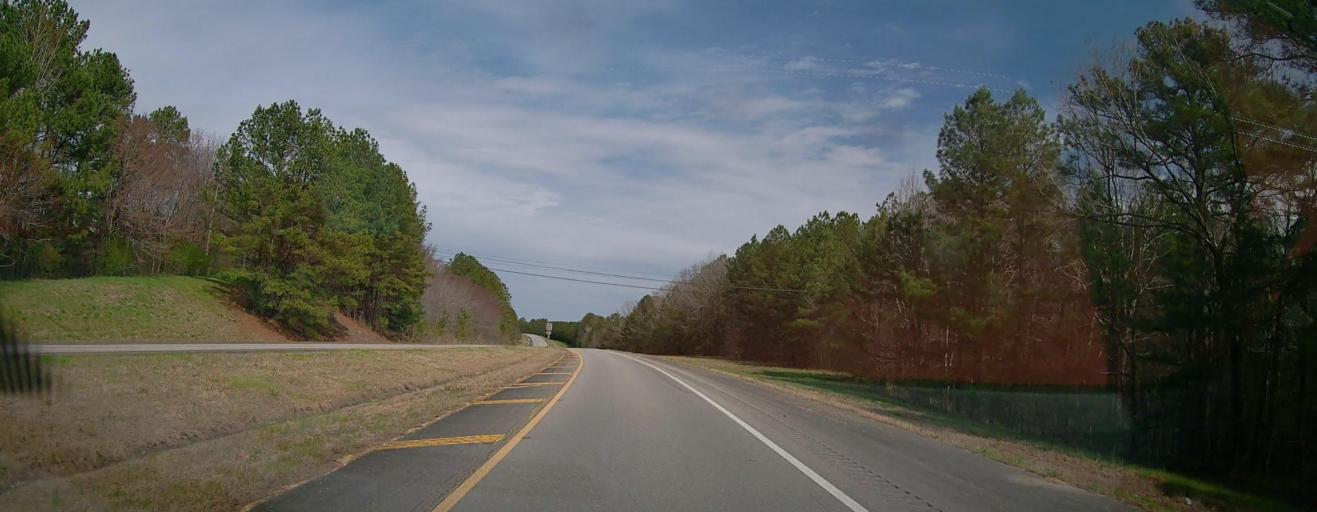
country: US
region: Alabama
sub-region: Marion County
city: Winfield
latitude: 33.9293
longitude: -87.6728
